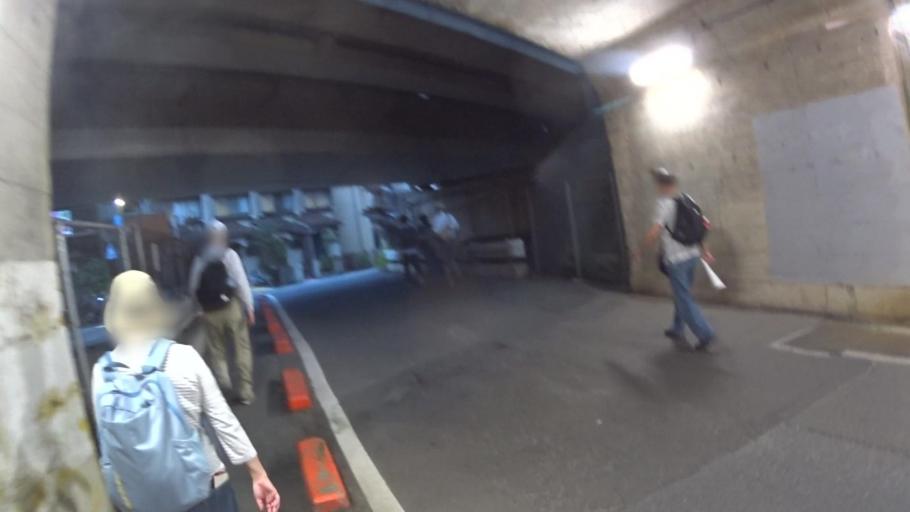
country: JP
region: Osaka
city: Kaizuka
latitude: 34.4429
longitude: 135.2755
